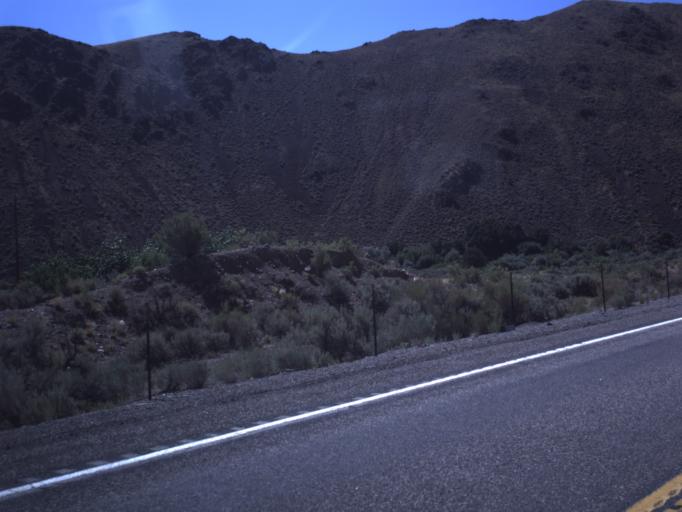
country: US
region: Utah
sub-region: Sevier County
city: Monroe
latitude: 38.4883
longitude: -112.2428
